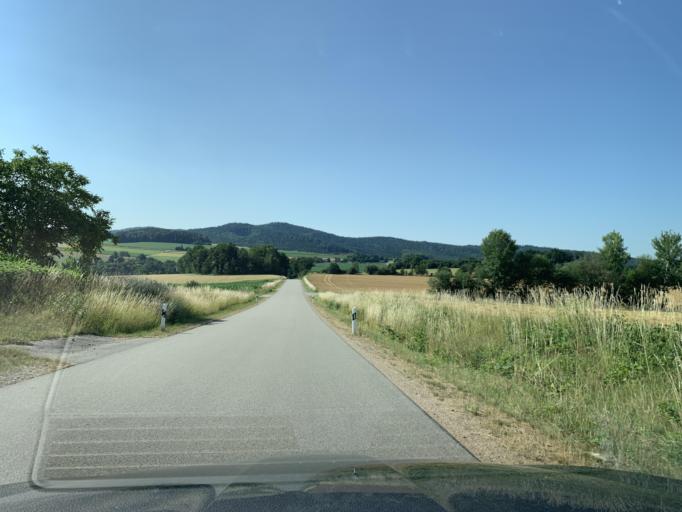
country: DE
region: Bavaria
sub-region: Upper Palatinate
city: Dieterskirchen
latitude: 49.4112
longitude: 12.4133
